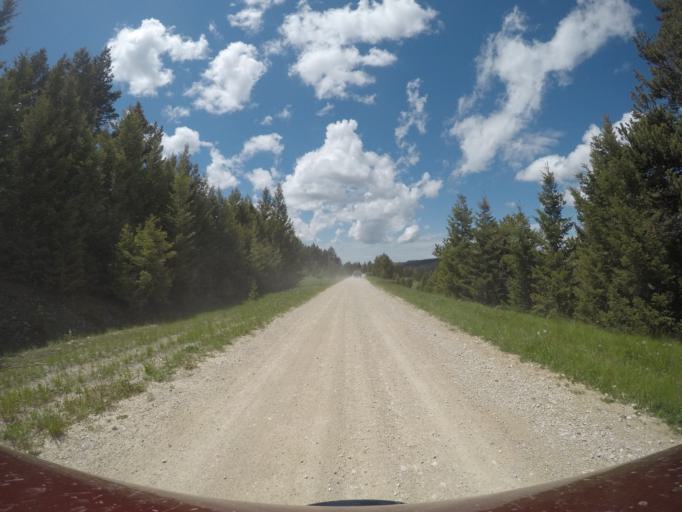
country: US
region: Wyoming
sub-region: Big Horn County
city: Lovell
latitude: 45.2013
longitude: -108.5100
